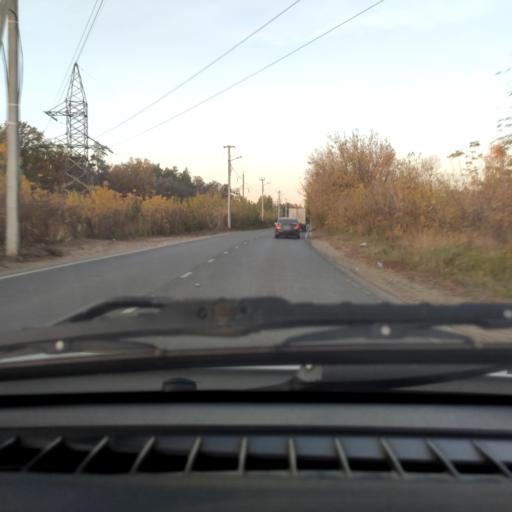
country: RU
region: Samara
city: Zhigulevsk
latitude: 53.5125
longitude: 49.4681
